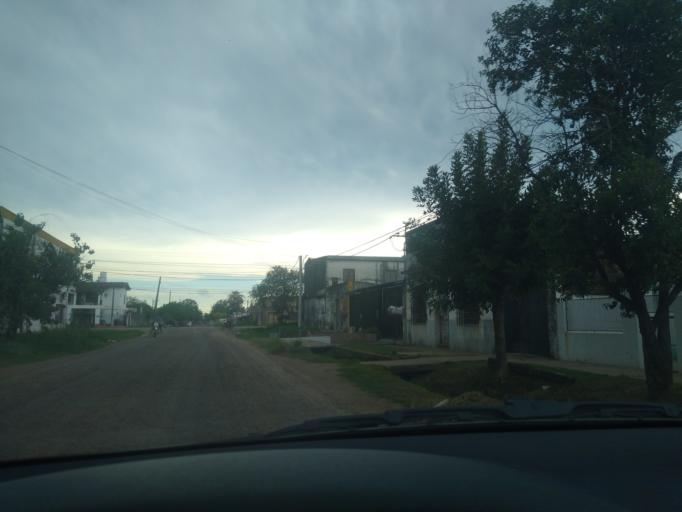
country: AR
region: Chaco
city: Barranqueras
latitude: -27.4882
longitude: -58.9438
